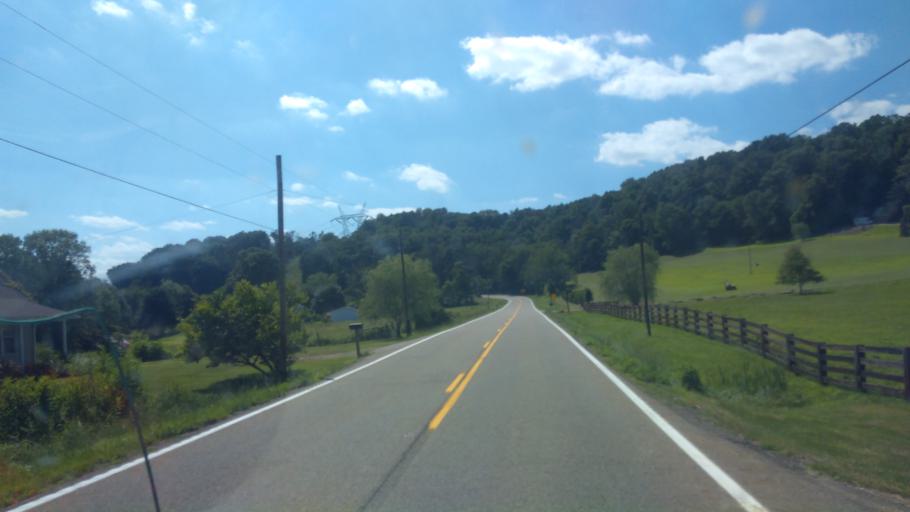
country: US
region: Ohio
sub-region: Carroll County
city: Carrollton
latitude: 40.5687
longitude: -81.1436
